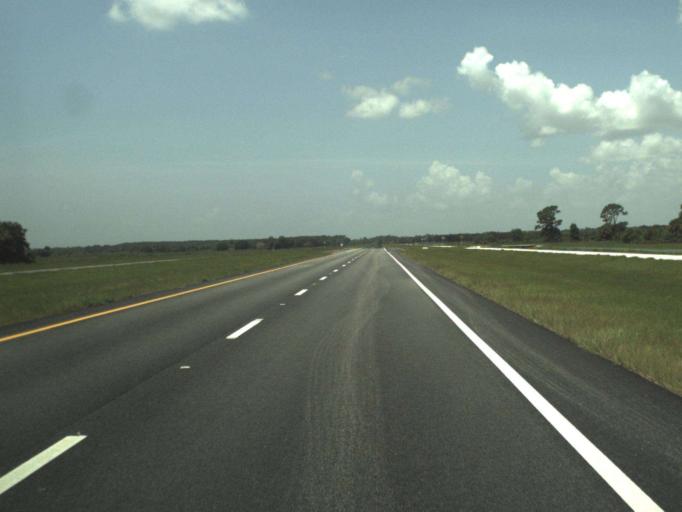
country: US
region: Florida
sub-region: Okeechobee County
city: Cypress Quarters
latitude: 27.3519
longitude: -80.6344
